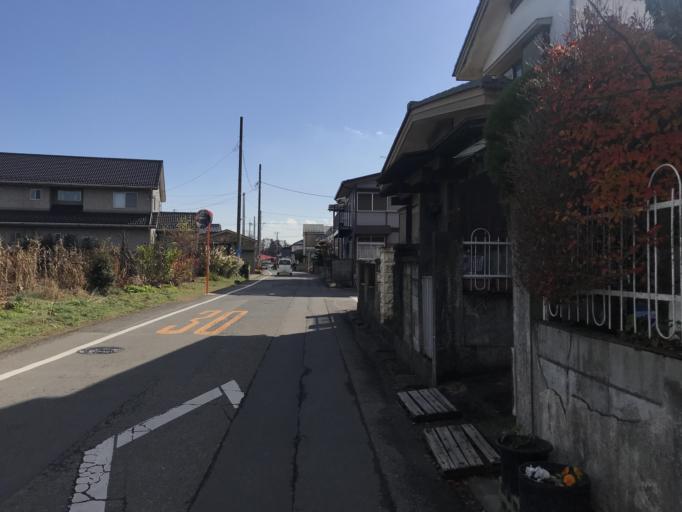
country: JP
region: Ibaraki
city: Ushiku
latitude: 35.9731
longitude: 140.1529
